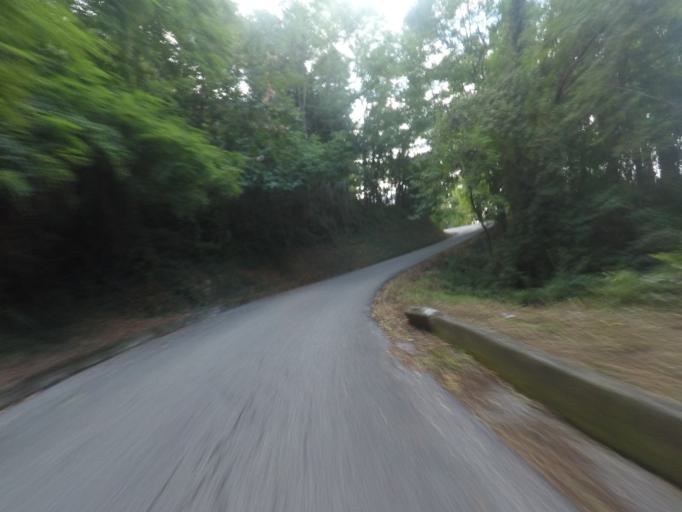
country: IT
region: Tuscany
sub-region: Provincia di Lucca
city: Massarosa
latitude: 43.9110
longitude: 10.3655
